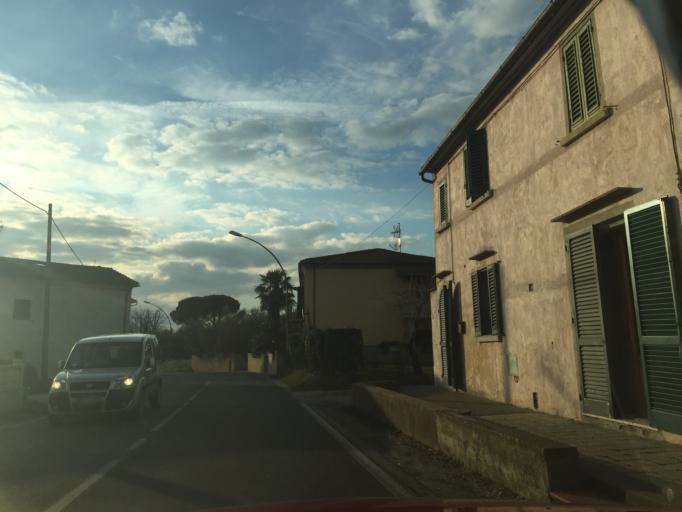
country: IT
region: Tuscany
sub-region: Provincia di Pistoia
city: San Rocco
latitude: 43.8251
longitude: 10.8727
